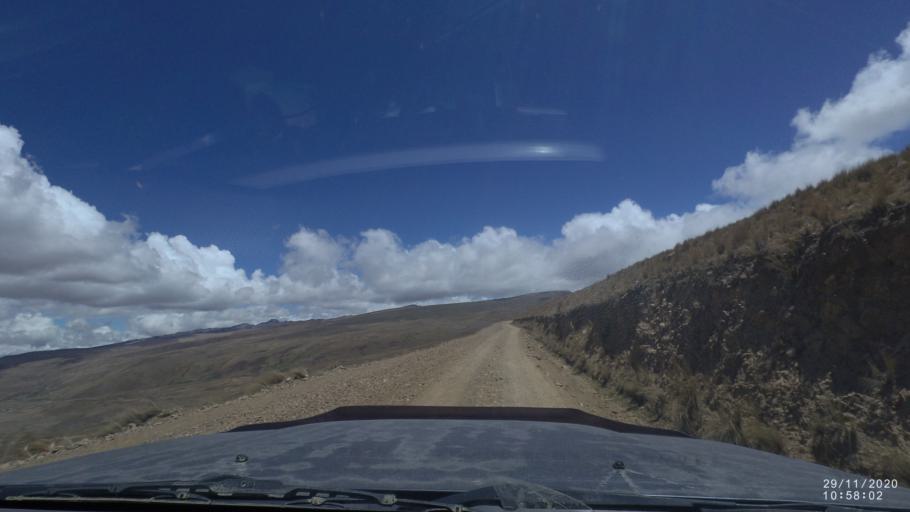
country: BO
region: Cochabamba
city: Cochabamba
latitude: -17.2121
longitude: -66.2317
